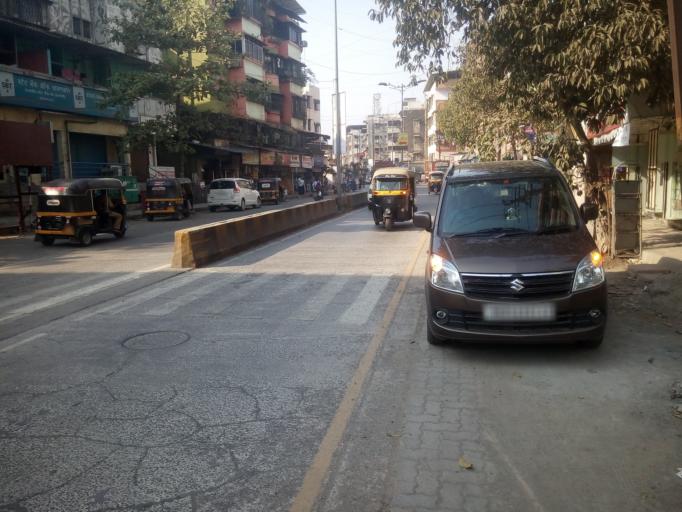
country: IN
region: Maharashtra
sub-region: Thane
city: Dombivli
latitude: 19.2087
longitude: 73.0941
